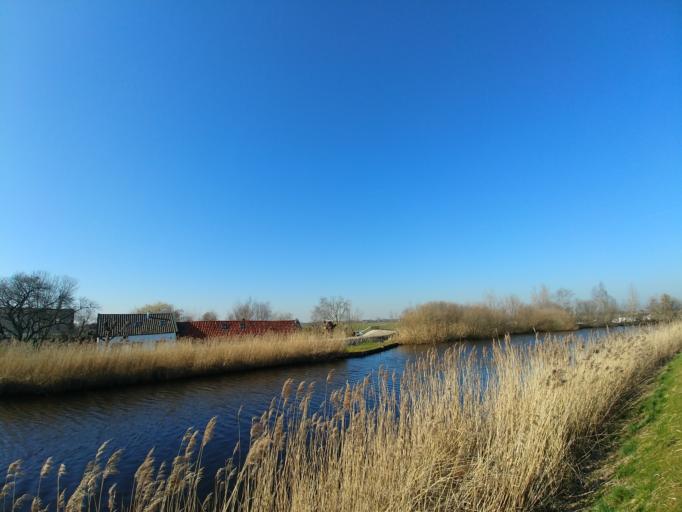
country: NL
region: Utrecht
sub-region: Gemeente Woerden
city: Woerden
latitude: 52.1378
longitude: 4.8712
